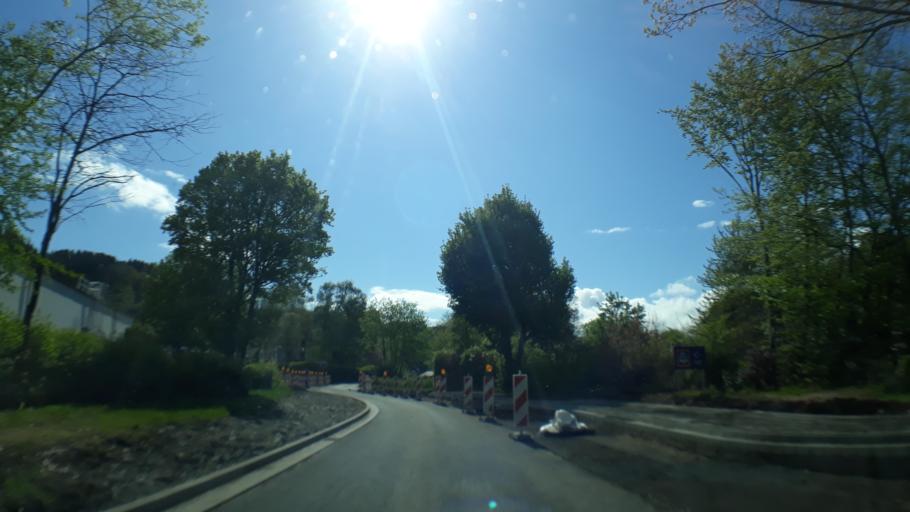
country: DE
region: North Rhine-Westphalia
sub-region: Regierungsbezirk Koln
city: Hellenthal
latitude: 50.4897
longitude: 6.4515
